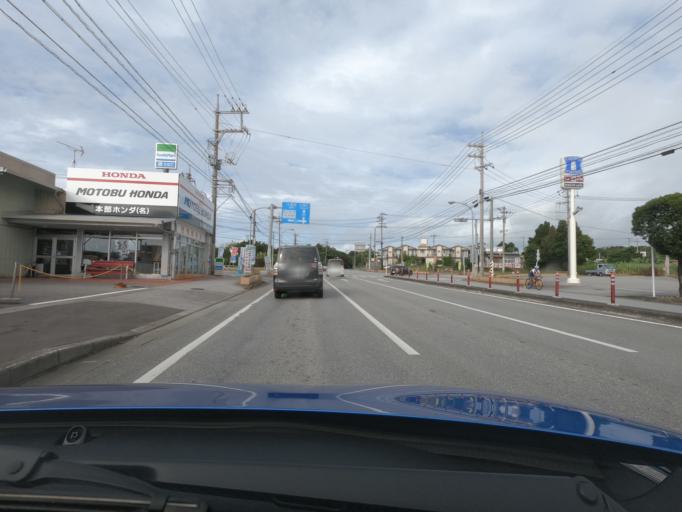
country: JP
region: Okinawa
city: Nago
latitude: 26.6773
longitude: 127.8914
